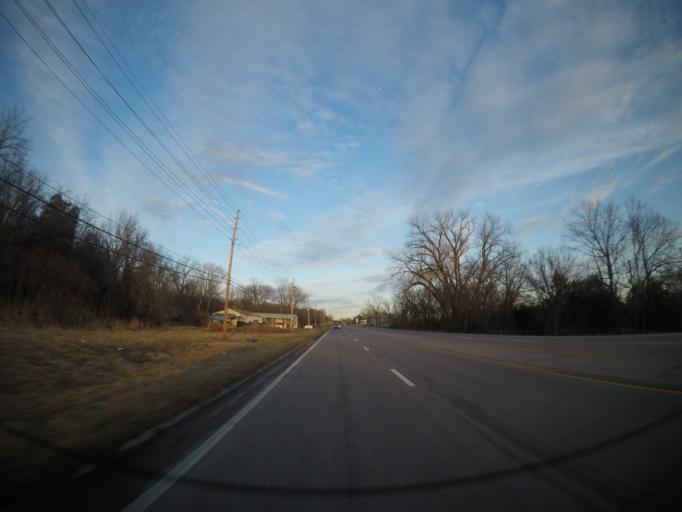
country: US
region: Kansas
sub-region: Wyandotte County
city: Edwardsville
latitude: 39.0611
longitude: -94.8100
